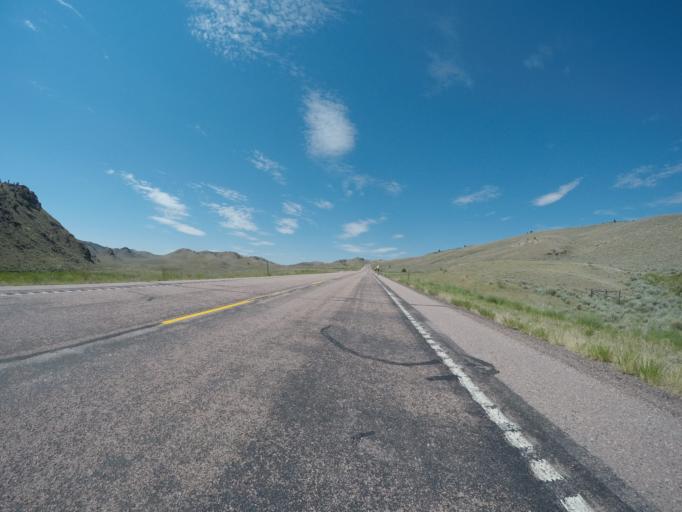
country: US
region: Wyoming
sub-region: Albany County
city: Laramie
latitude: 41.6924
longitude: -105.5097
